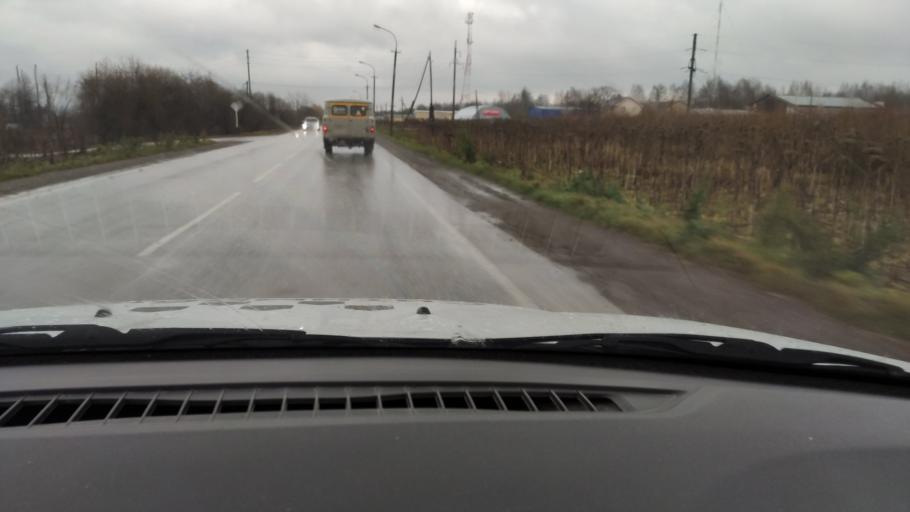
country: RU
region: Perm
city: Sylva
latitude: 58.0271
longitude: 56.7248
